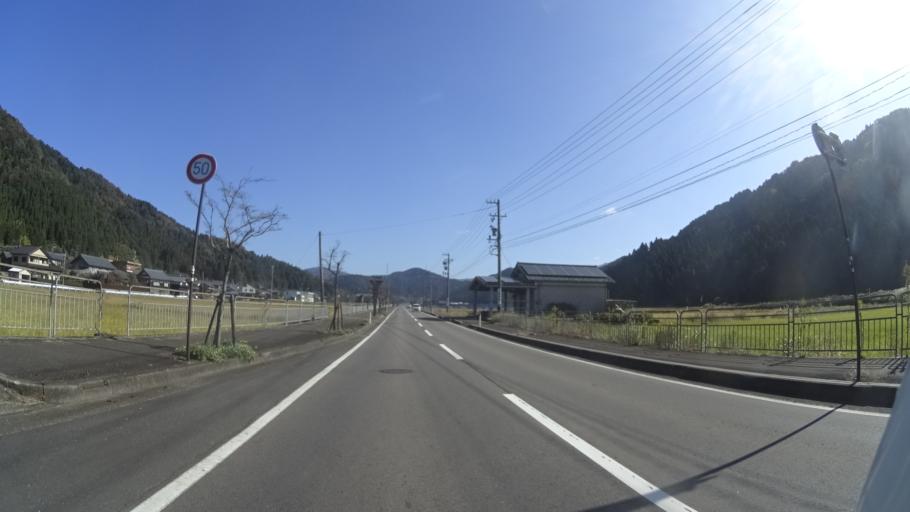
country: JP
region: Fukui
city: Sabae
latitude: 35.9479
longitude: 136.2538
